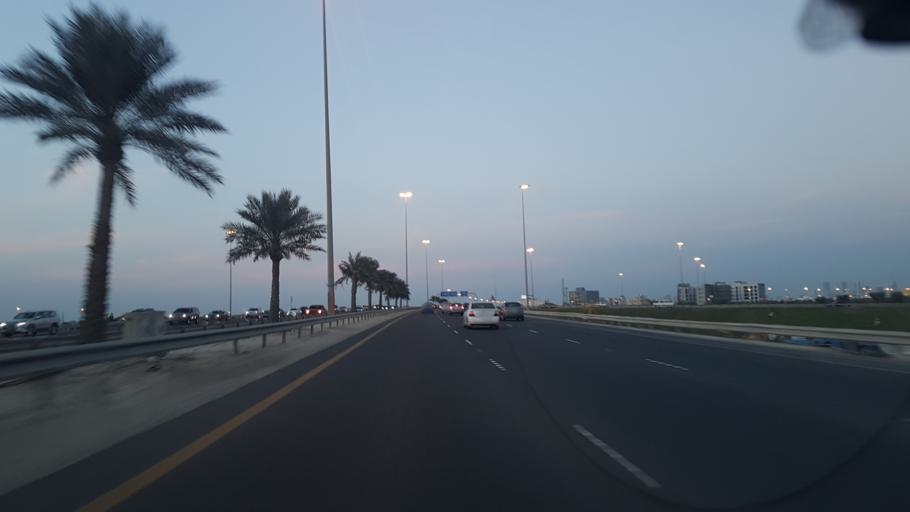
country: BH
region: Northern
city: Madinat `Isa
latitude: 26.1827
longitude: 50.5028
